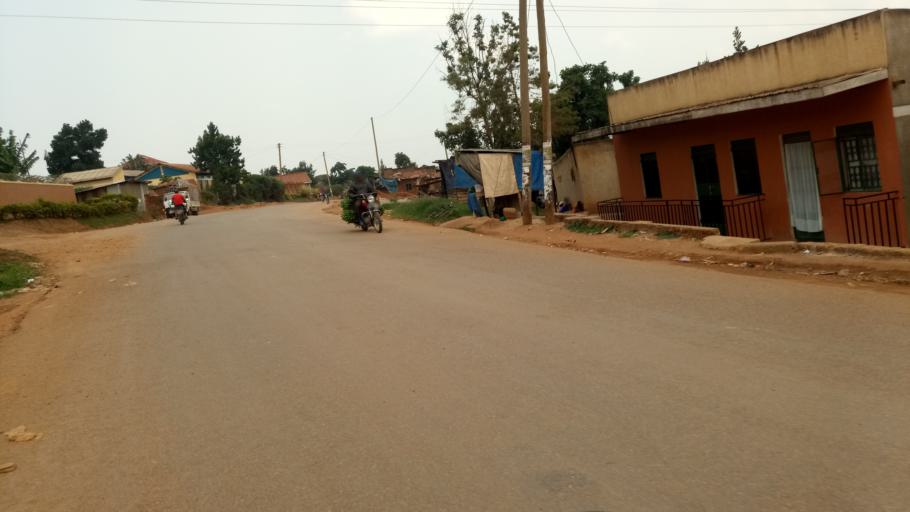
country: UG
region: Western Region
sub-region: Mbarara District
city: Mbarara
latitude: -0.6130
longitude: 30.6659
